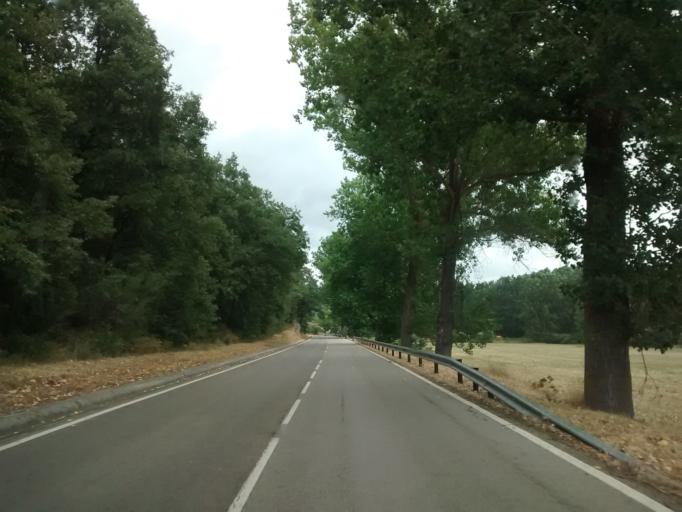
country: ES
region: Castille and Leon
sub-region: Provincia de Palencia
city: Berzosilla
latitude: 42.7902
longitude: -3.9881
